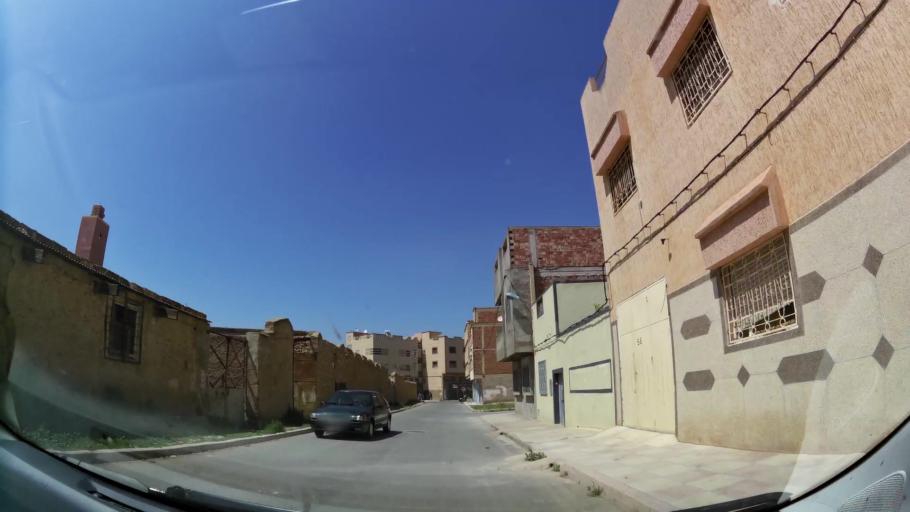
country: MA
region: Oriental
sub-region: Oujda-Angad
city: Oujda
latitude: 34.6921
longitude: -1.8854
